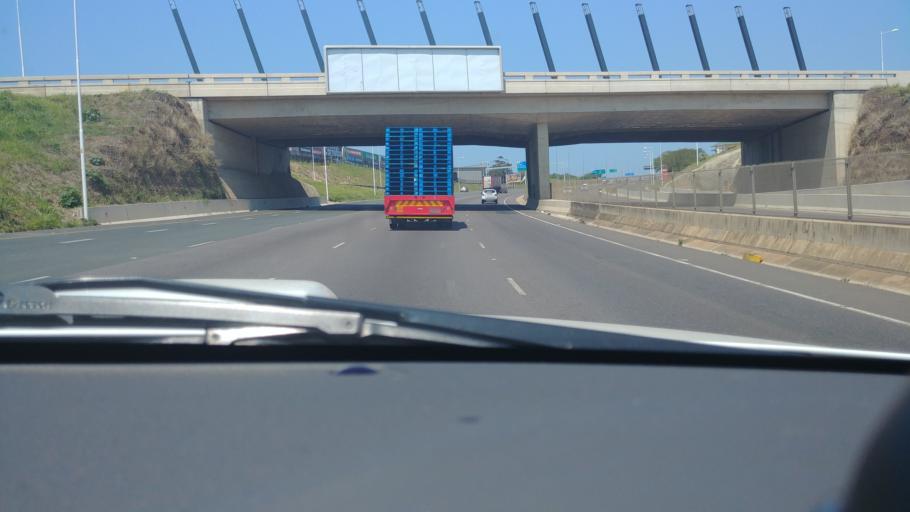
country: ZA
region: KwaZulu-Natal
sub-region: eThekwini Metropolitan Municipality
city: Durban
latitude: -29.7112
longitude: 31.0513
